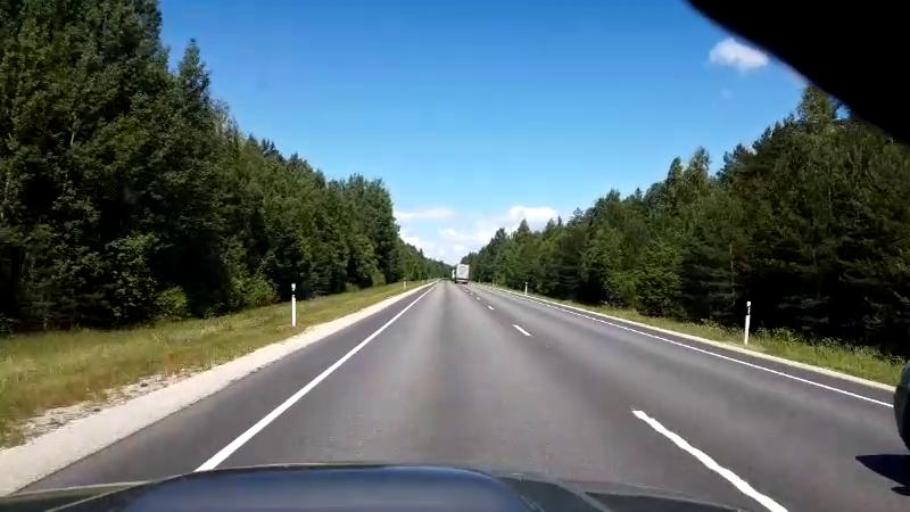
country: LV
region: Salacgrivas
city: Ainazi
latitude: 58.0998
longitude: 24.5081
